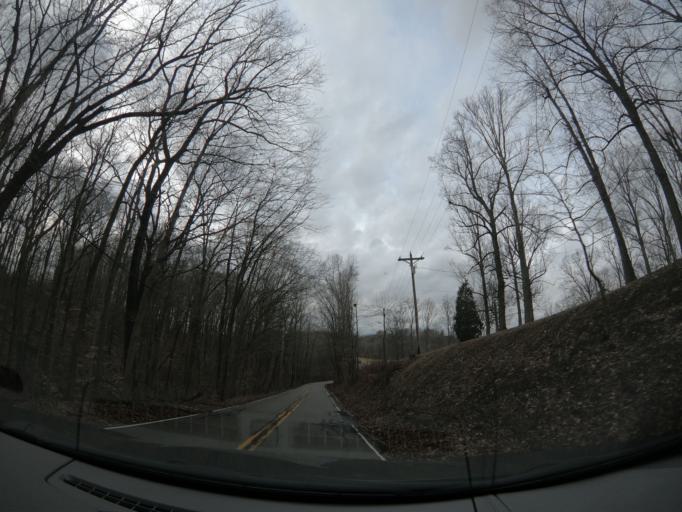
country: US
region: Indiana
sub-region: Floyd County
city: Galena
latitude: 38.3906
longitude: -85.9092
